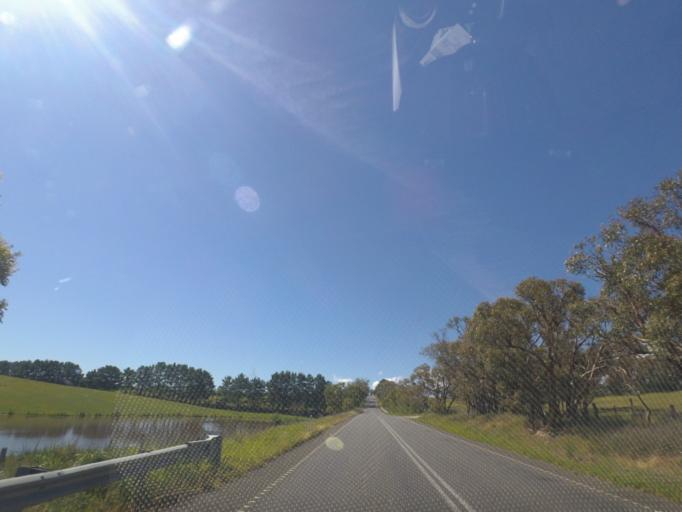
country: AU
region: Victoria
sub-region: Moorabool
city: Bacchus Marsh
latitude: -37.7868
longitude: 144.2145
